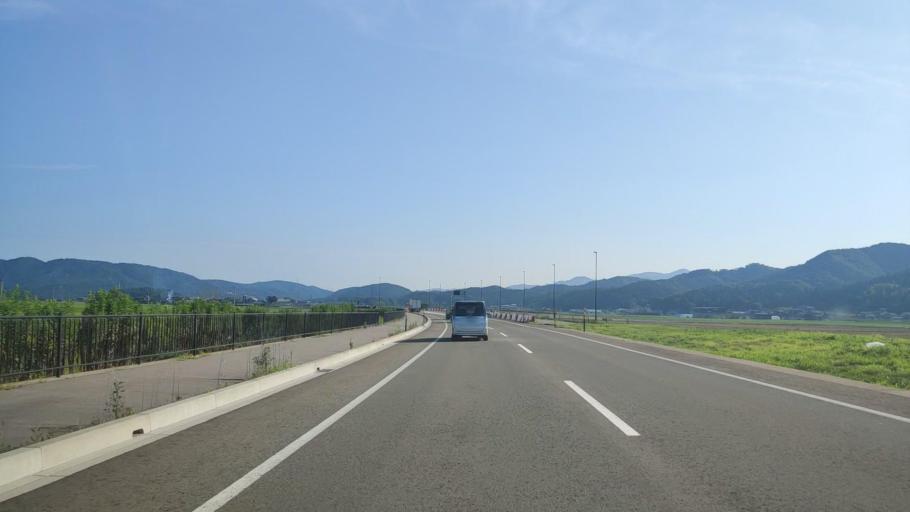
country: JP
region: Fukui
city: Maruoka
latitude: 36.1791
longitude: 136.2672
